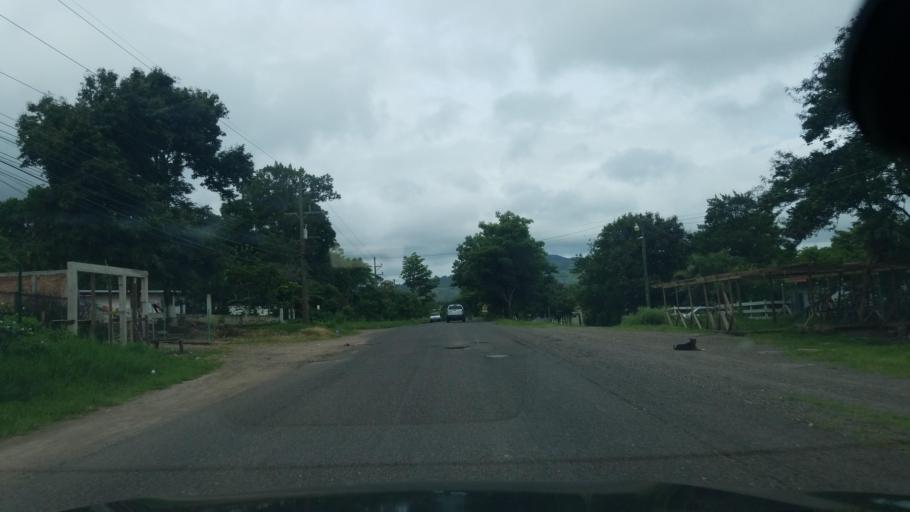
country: HN
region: Choluteca
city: San Marcos de Colon
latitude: 13.4135
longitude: -86.8403
